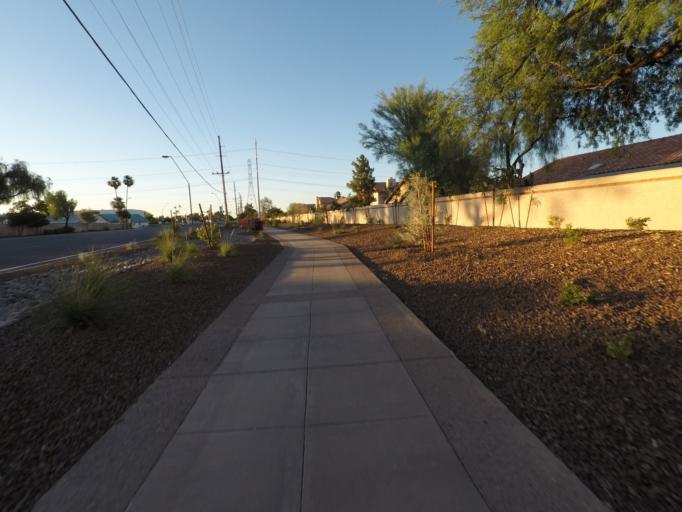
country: US
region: Arizona
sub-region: Maricopa County
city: Guadalupe
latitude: 33.3544
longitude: -111.9283
